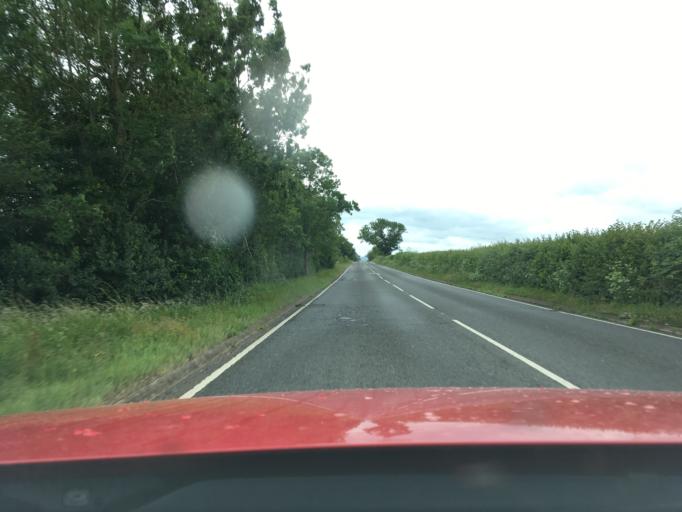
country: GB
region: England
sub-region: Warwickshire
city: Shipston on Stour
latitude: 52.1219
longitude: -1.6071
